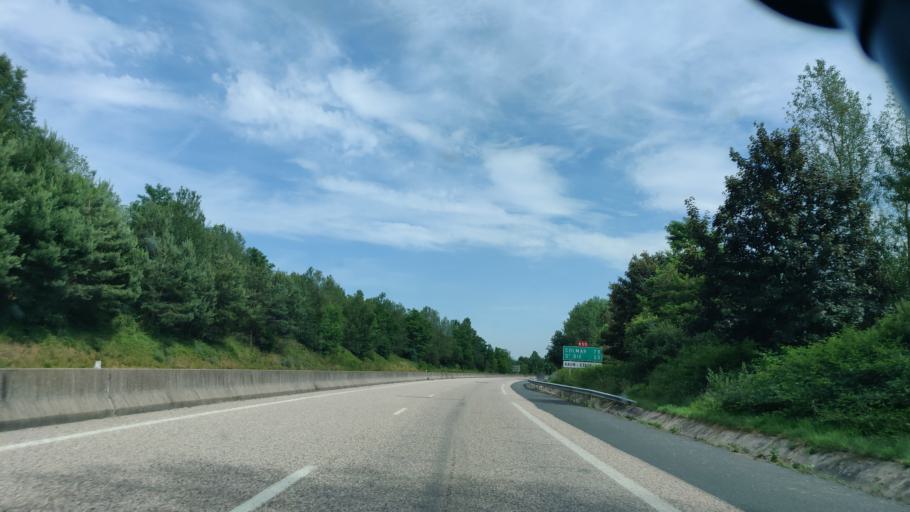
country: FR
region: Lorraine
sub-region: Departement de Meurthe-et-Moselle
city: Baccarat
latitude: 48.4361
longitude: 6.7787
